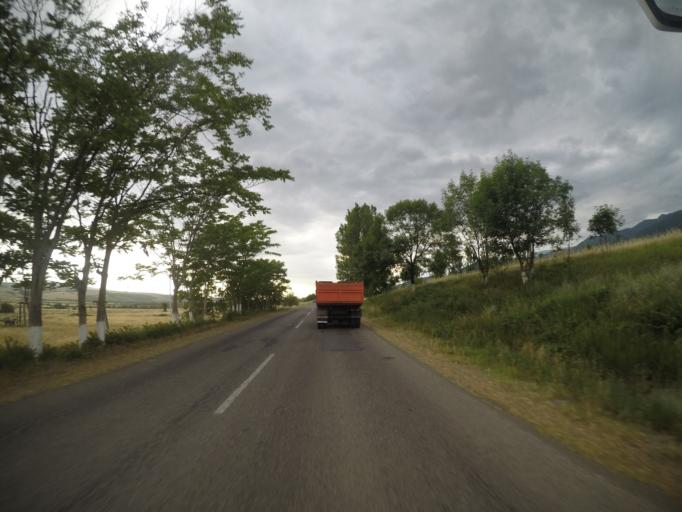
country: AZ
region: Ismayilli
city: Ismayilli
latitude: 40.7427
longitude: 48.2546
